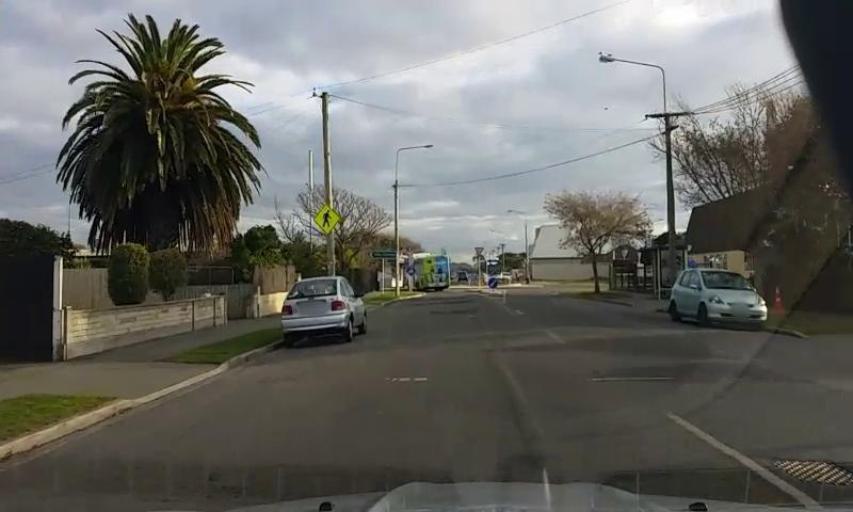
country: NZ
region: Canterbury
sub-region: Christchurch City
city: Christchurch
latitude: -43.5240
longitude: 172.7330
